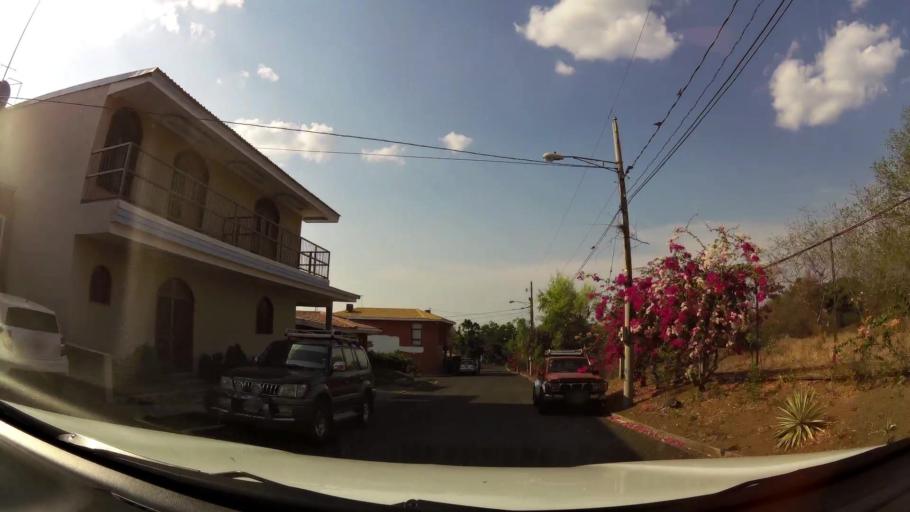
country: NI
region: Managua
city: Managua
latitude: 12.1026
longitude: -86.2710
